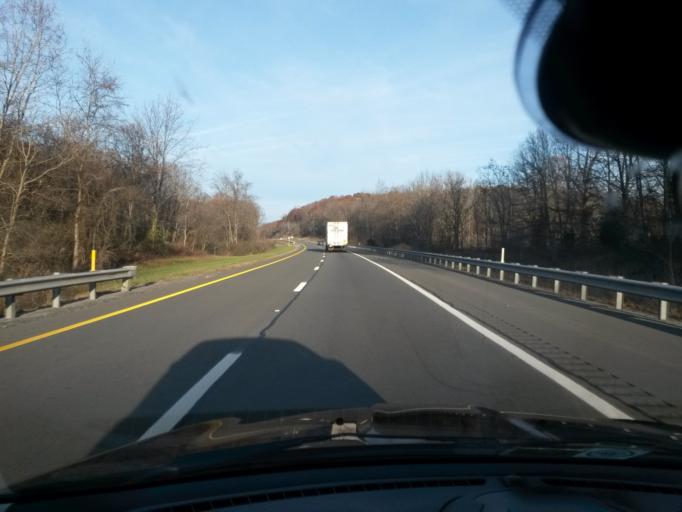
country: US
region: West Virginia
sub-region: Greenbrier County
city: Lewisburg
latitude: 37.8270
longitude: -80.4462
